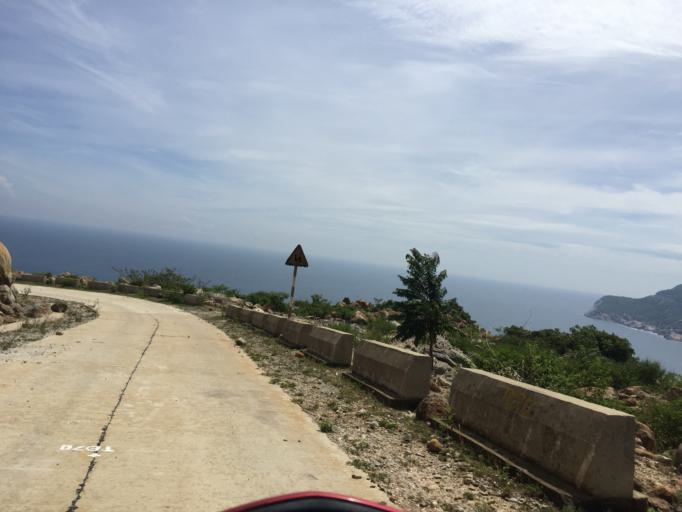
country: VN
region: Quang Nam
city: Hoi An
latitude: 15.9731
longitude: 108.5082
